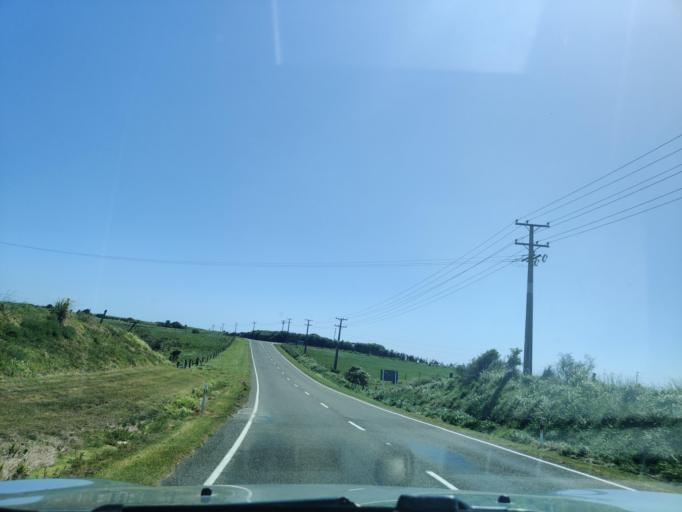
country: NZ
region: Taranaki
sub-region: South Taranaki District
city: Opunake
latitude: -39.4453
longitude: 173.8442
